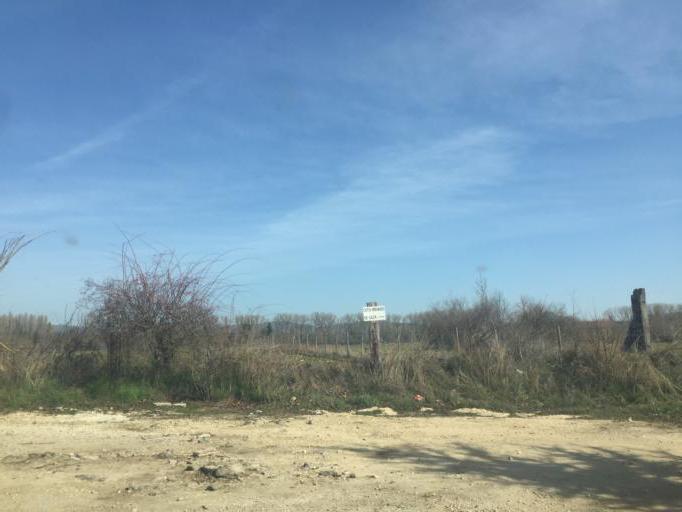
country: ES
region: Castille and Leon
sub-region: Provincia de Burgos
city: Medina de Pomar
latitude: 42.9388
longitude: -3.5829
